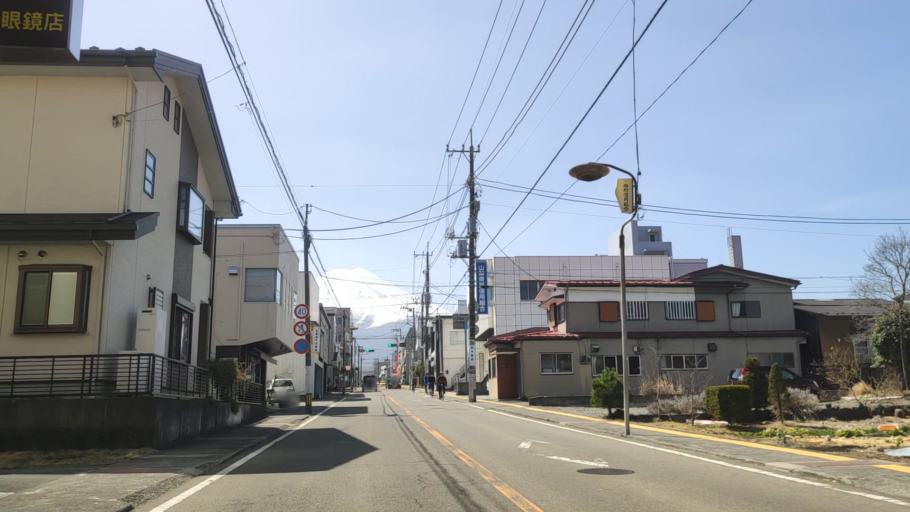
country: JP
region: Yamanashi
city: Fujikawaguchiko
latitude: 35.4887
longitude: 138.8015
